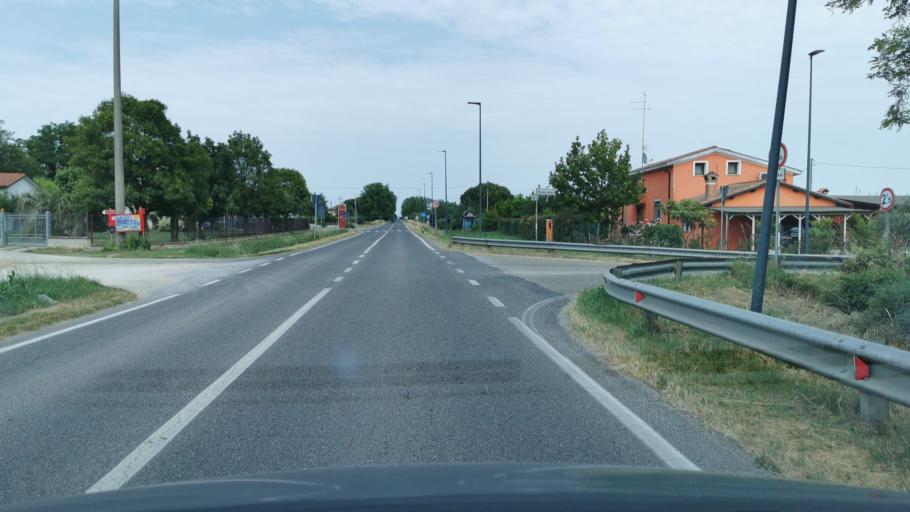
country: IT
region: Emilia-Romagna
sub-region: Provincia di Ravenna
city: Savarna-Conventella
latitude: 44.5330
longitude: 12.1232
